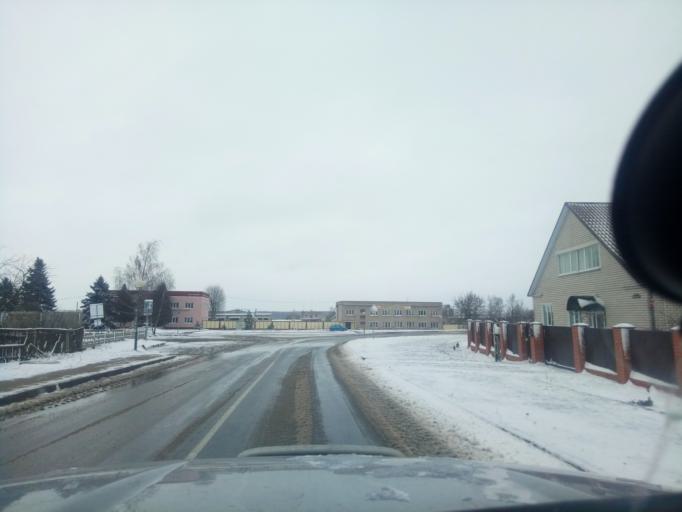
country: BY
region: Minsk
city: Kapyl'
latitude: 53.1426
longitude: 27.0951
